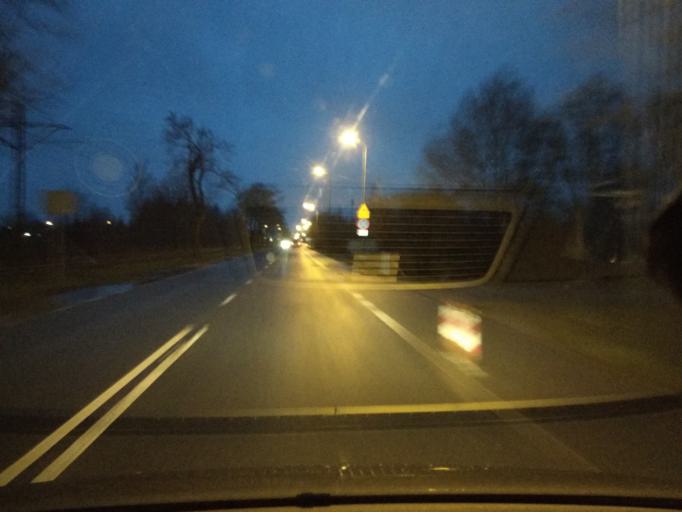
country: PL
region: Lower Silesian Voivodeship
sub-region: Powiat wroclawski
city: Smolec
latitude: 51.1422
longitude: 16.9043
